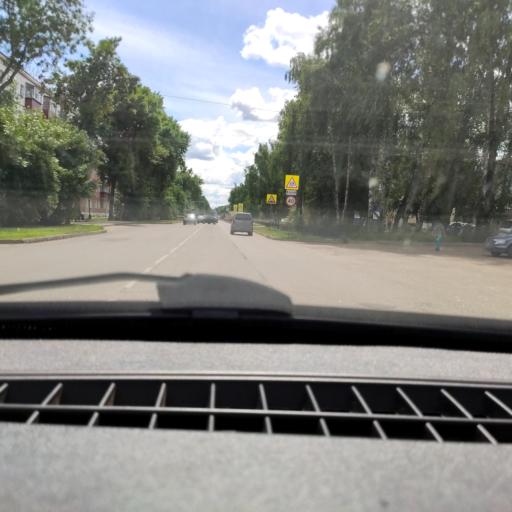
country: RU
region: Bashkortostan
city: Sterlitamak
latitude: 53.6424
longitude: 55.9333
